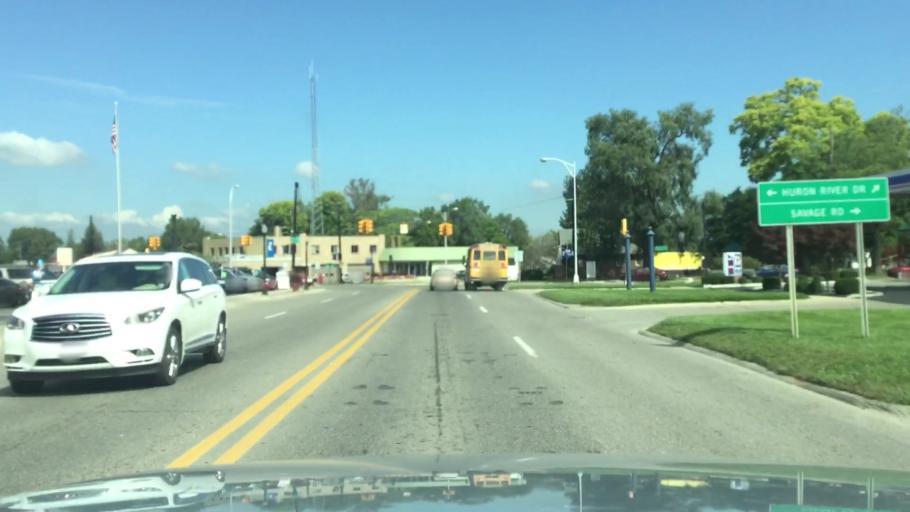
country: US
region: Michigan
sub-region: Wayne County
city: Belleville
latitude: 42.2039
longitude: -83.4852
